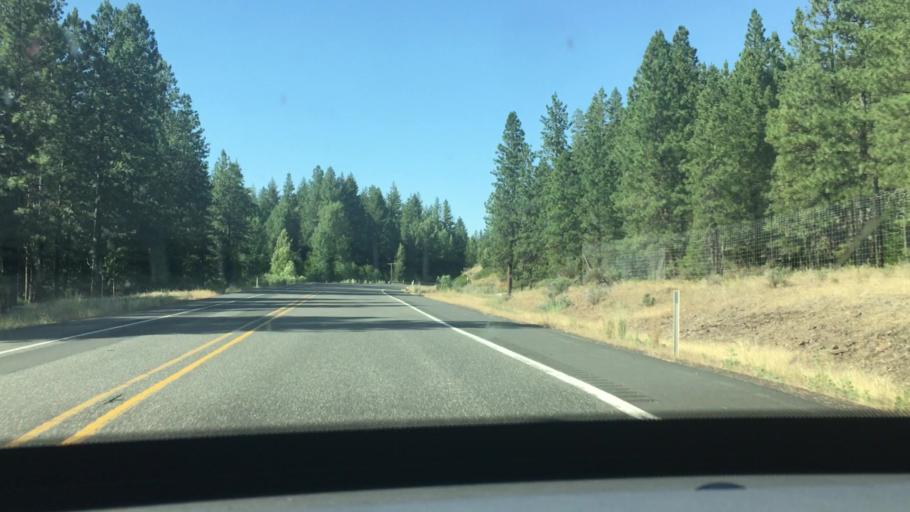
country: US
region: Washington
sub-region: Klickitat County
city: Goldendale
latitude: 45.9167
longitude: -120.7052
